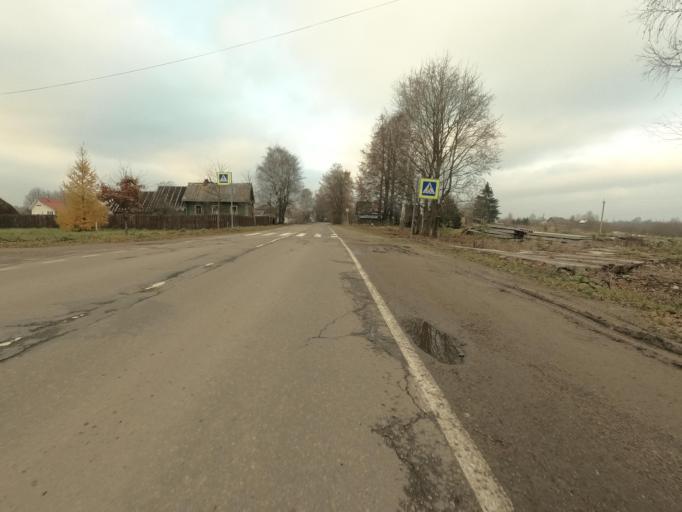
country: RU
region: Leningrad
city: Mga
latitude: 59.7827
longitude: 31.0243
